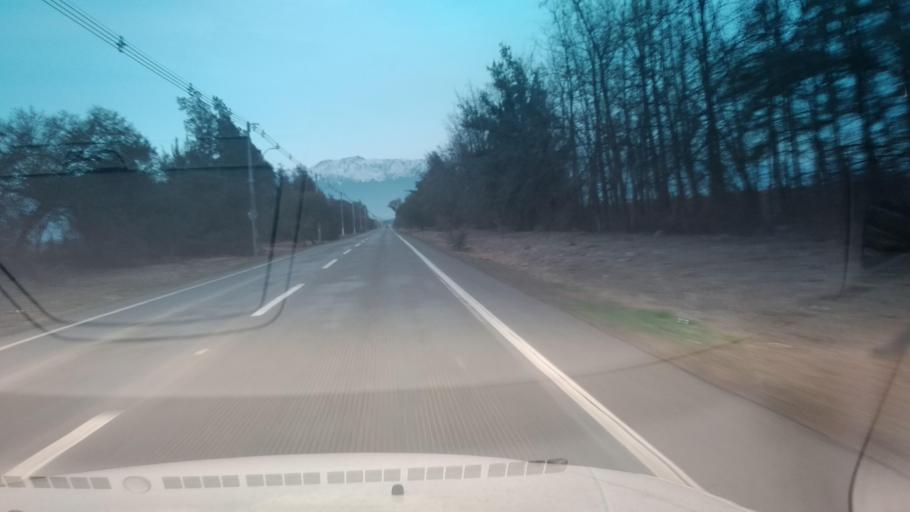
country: CL
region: Santiago Metropolitan
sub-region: Provincia de Chacabuco
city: Chicureo Abajo
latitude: -33.0941
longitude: -70.7051
